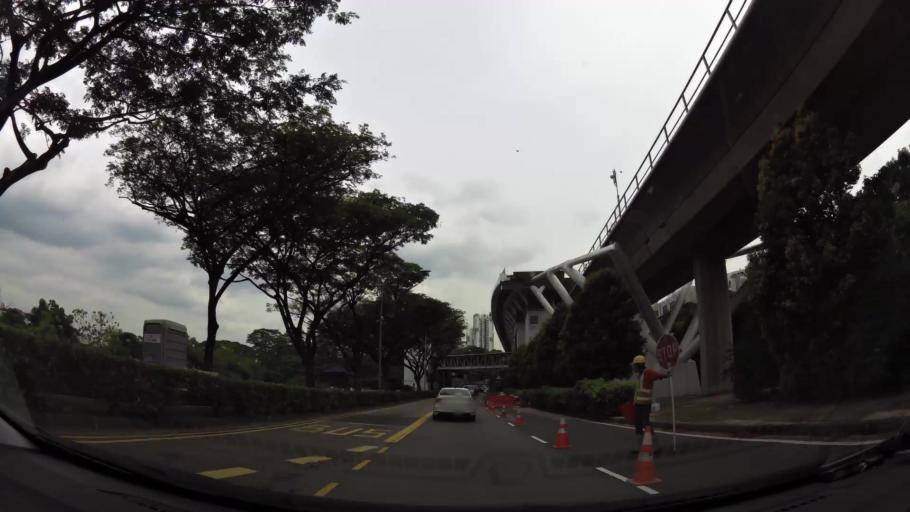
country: SG
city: Singapore
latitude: 1.3122
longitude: 103.7776
